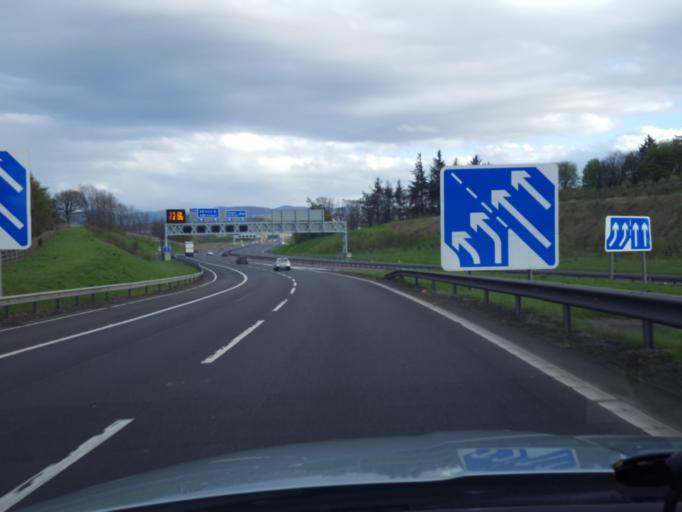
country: GB
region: Scotland
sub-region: Edinburgh
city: Kirkliston
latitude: 55.9550
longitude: -3.4170
